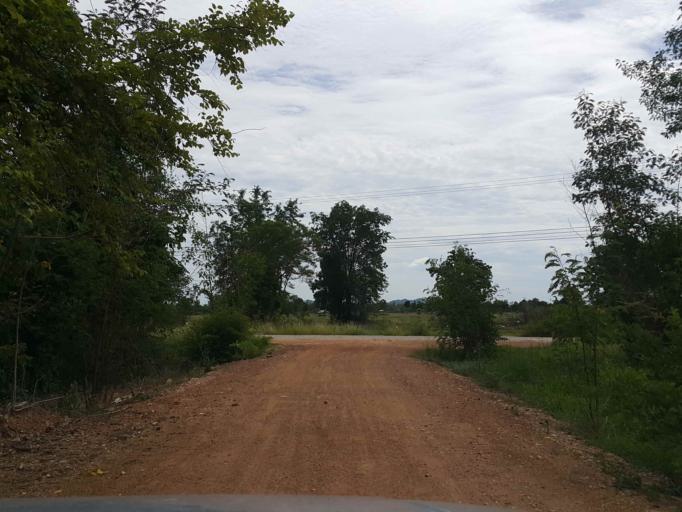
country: TH
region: Sukhothai
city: Ban Dan Lan Hoi
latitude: 17.0932
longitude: 99.4758
